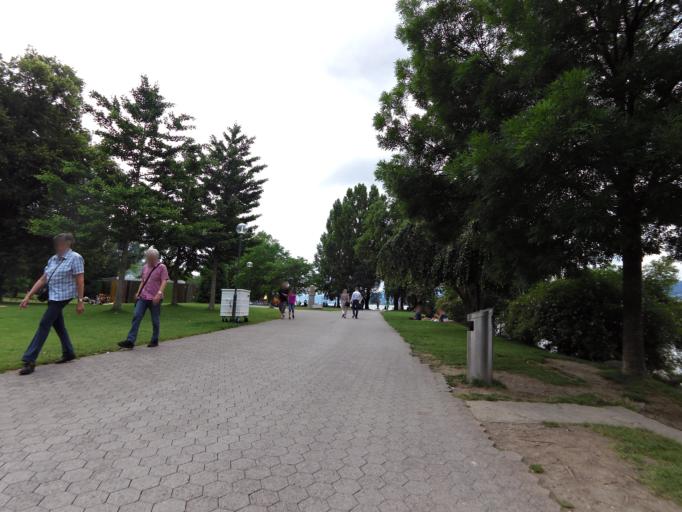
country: CH
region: Zurich
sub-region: Bezirk Zuerich
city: Zurich
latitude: 47.3586
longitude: 8.5473
